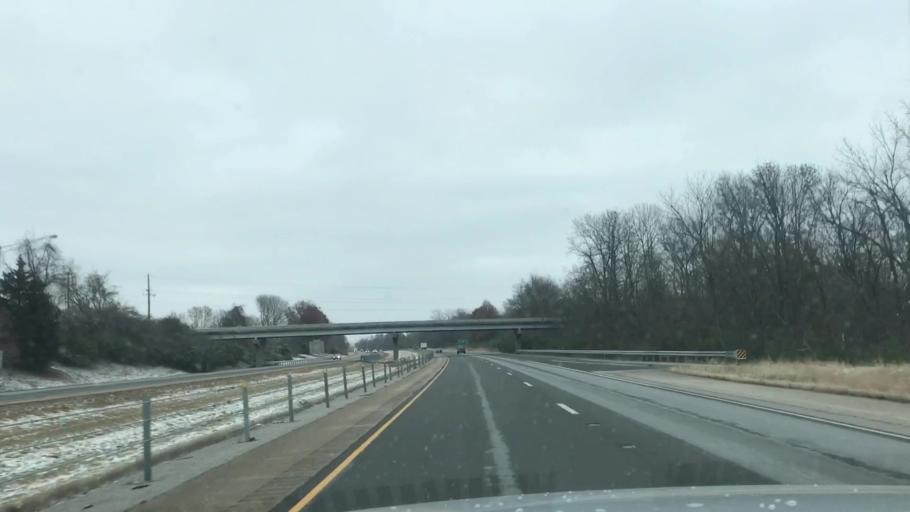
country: US
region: Illinois
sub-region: Madison County
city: Glen Carbon
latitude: 38.7548
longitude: -89.9537
